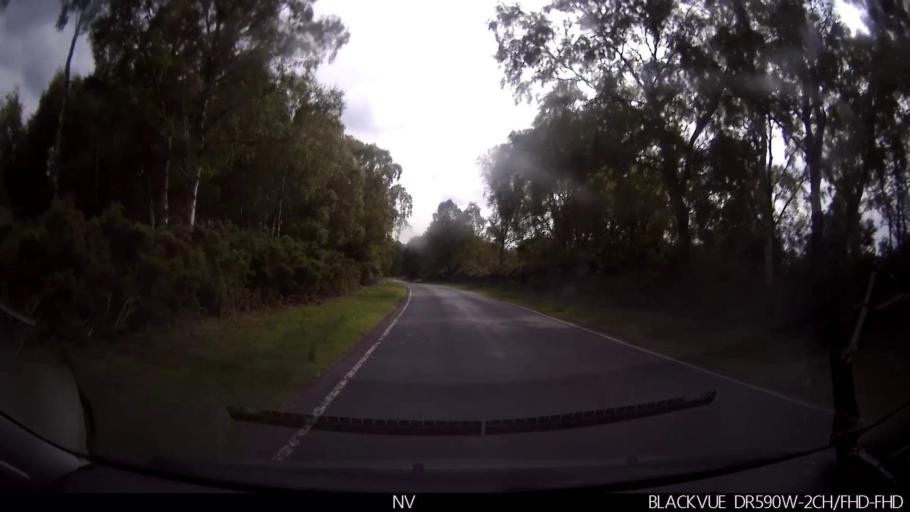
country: GB
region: England
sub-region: North Yorkshire
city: Strensall
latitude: 54.0451
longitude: -1.0084
